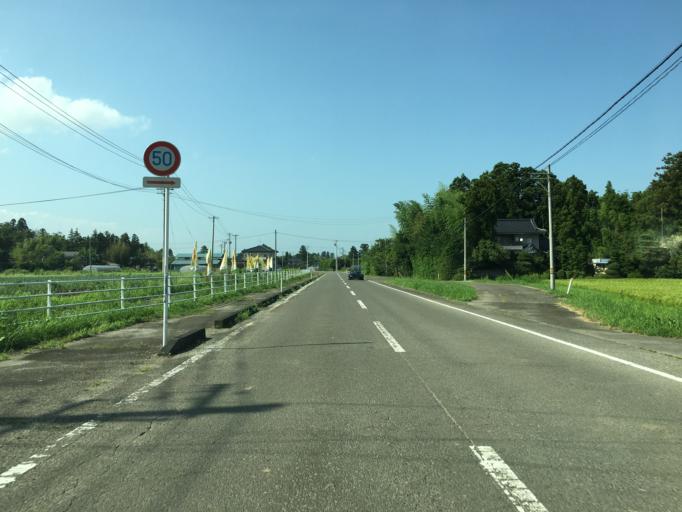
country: JP
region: Miyagi
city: Kakuda
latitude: 37.9451
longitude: 140.7987
